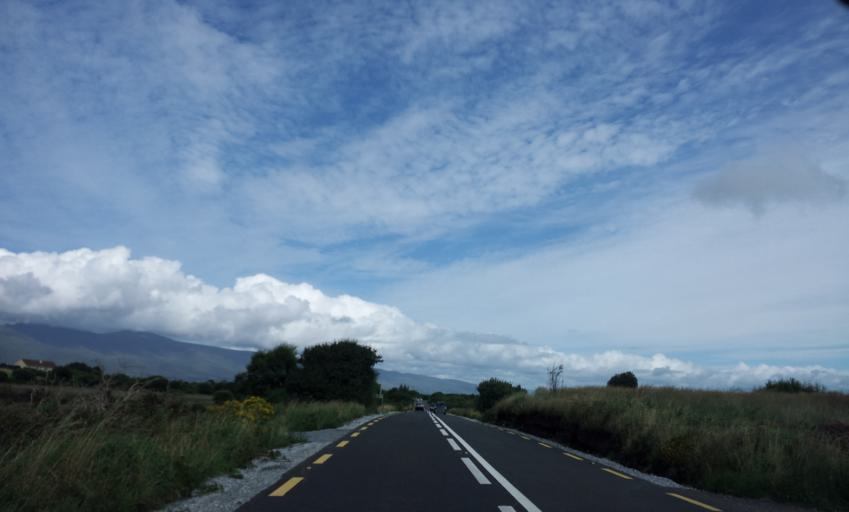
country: IE
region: Munster
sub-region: Ciarrai
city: Killorglin
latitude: 52.0773
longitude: -9.8779
